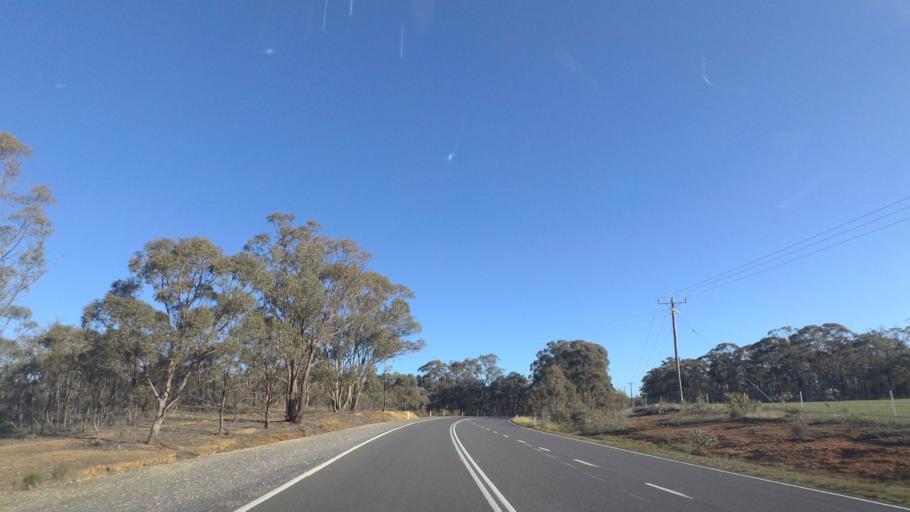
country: AU
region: Victoria
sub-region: Greater Bendigo
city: Kennington
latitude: -36.8726
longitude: 144.4983
